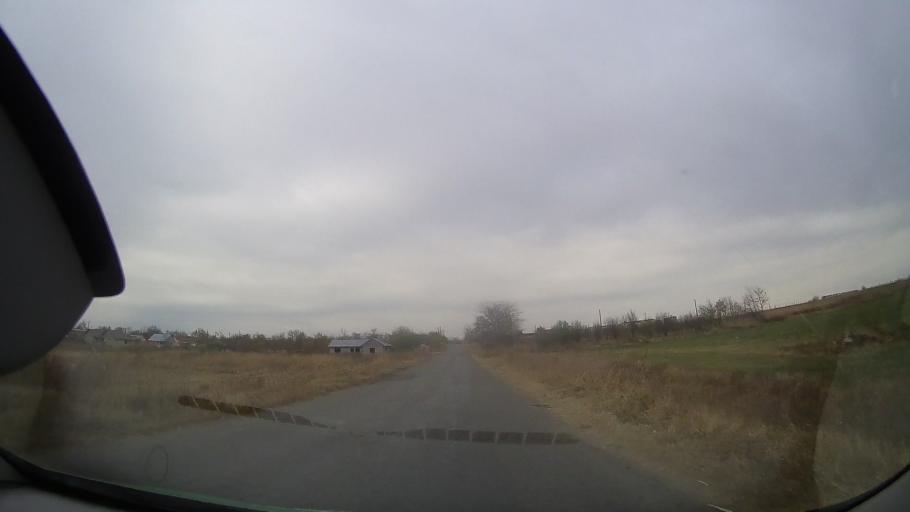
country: RO
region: Buzau
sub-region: Comuna Largu
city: Largu
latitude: 44.9743
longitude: 27.1555
